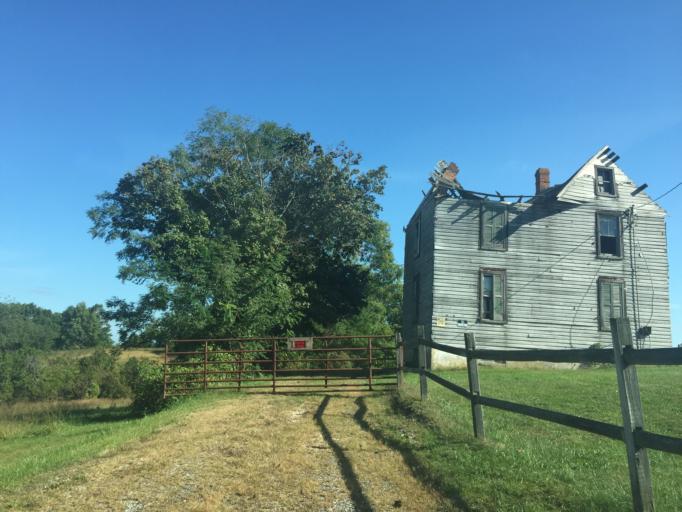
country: US
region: Maryland
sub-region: Baltimore County
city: Perry Hall
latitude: 39.3770
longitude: -76.4757
